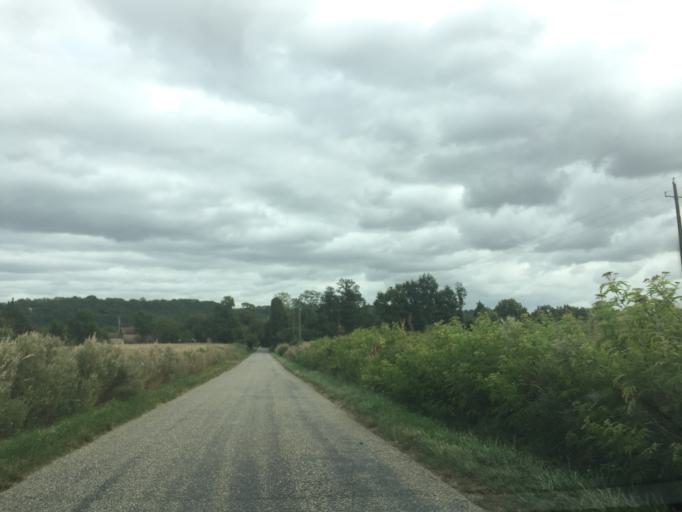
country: FR
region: Midi-Pyrenees
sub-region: Departement du Gers
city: Jegun
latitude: 43.6683
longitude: 0.3896
